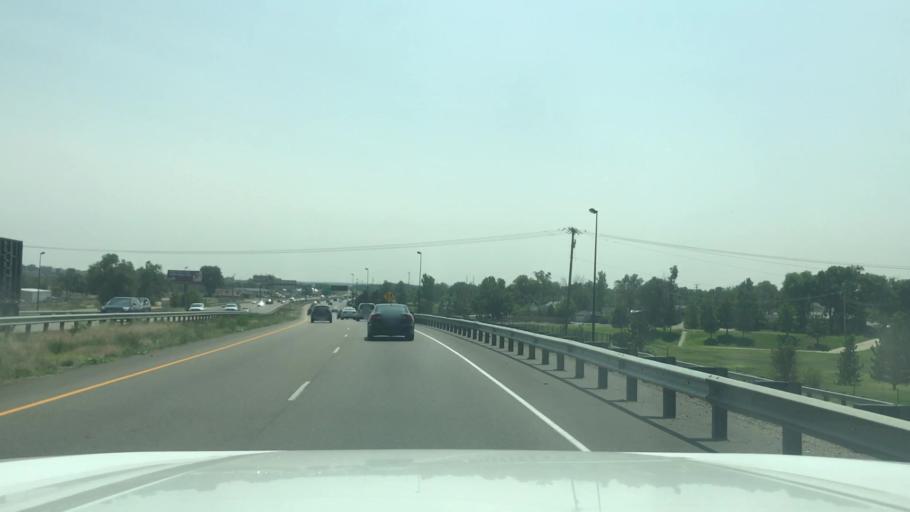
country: US
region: Colorado
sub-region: Pueblo County
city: Pueblo
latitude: 38.2976
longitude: -104.6129
